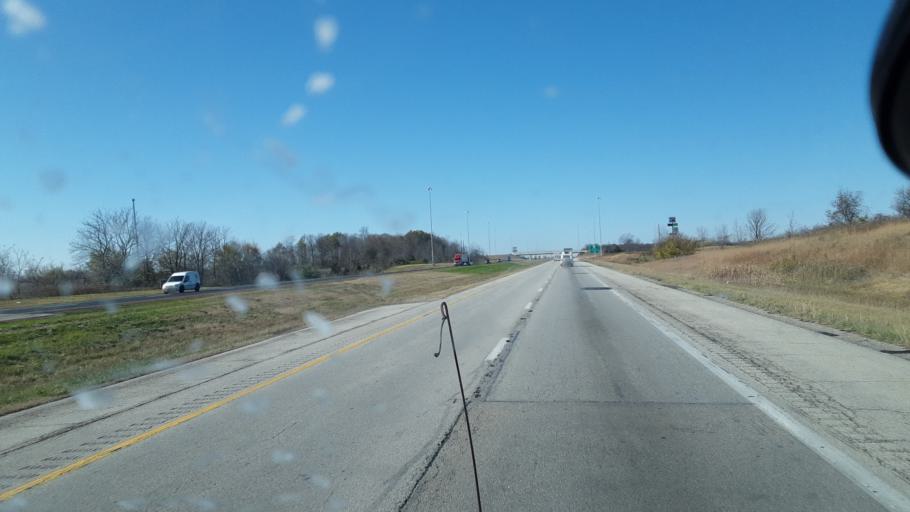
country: US
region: Ohio
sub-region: Preble County
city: Lewisburg
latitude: 39.8359
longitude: -84.6182
